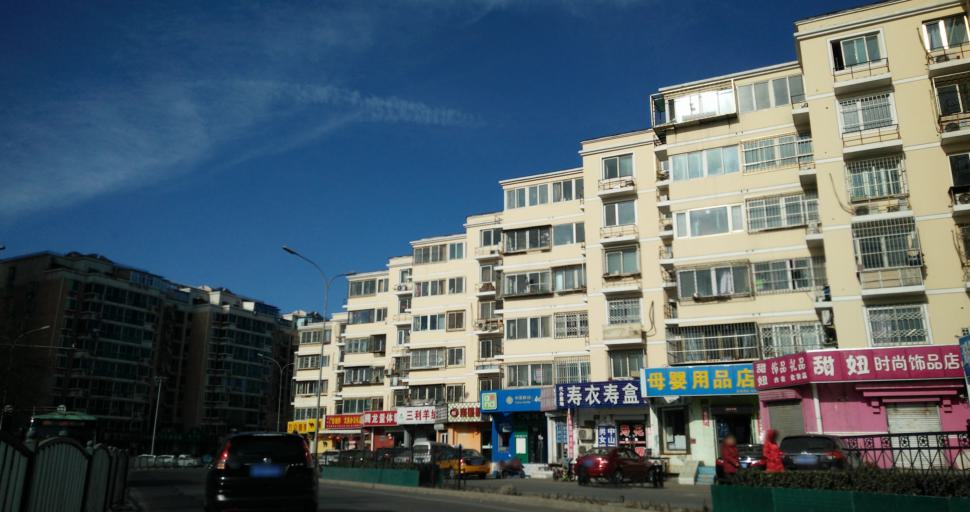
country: CN
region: Beijing
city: Daxing
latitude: 39.7444
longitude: 116.3331
